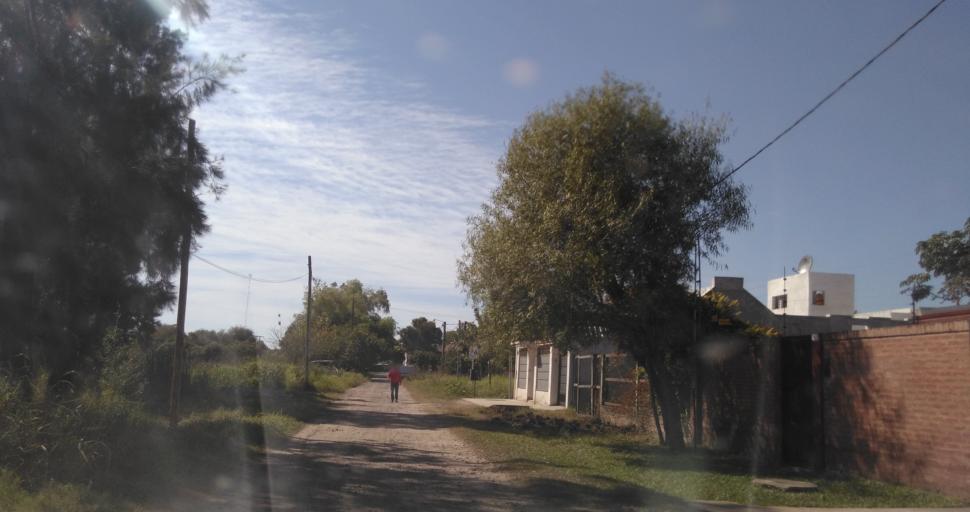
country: AR
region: Chaco
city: Fontana
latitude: -27.4402
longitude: -59.0240
